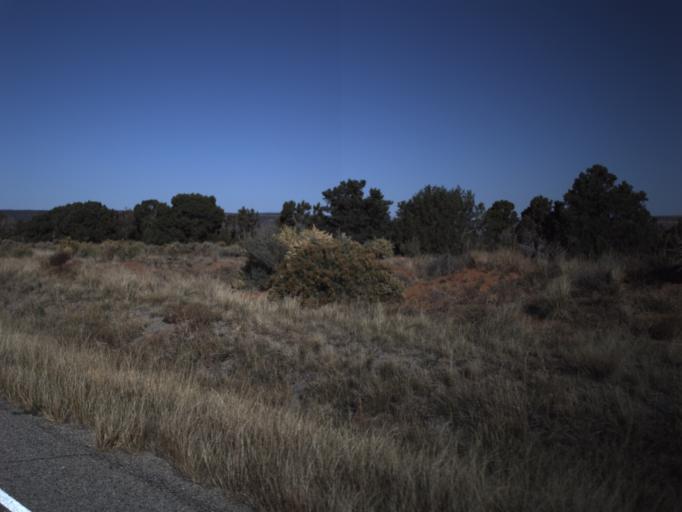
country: US
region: Utah
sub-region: San Juan County
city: Blanding
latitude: 37.5406
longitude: -109.9638
